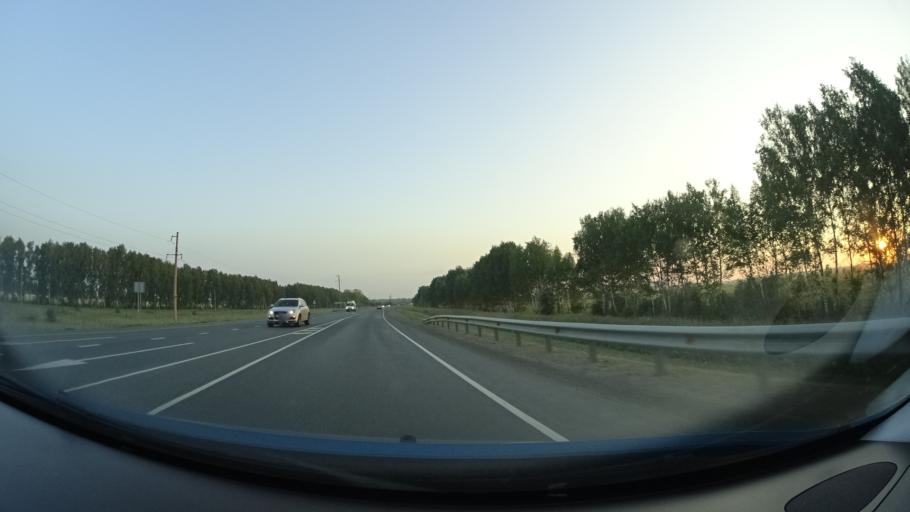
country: RU
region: Samara
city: Sernovodsk
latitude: 53.8939
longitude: 51.2653
